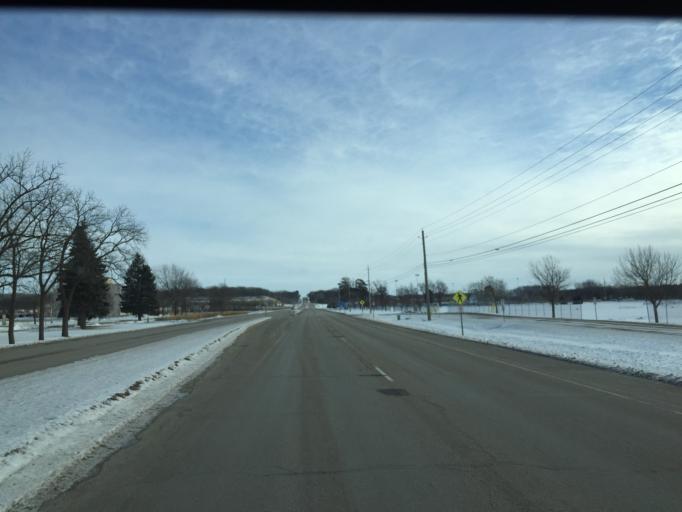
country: US
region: Minnesota
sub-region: Olmsted County
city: Rochester
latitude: 44.0215
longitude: -92.4339
